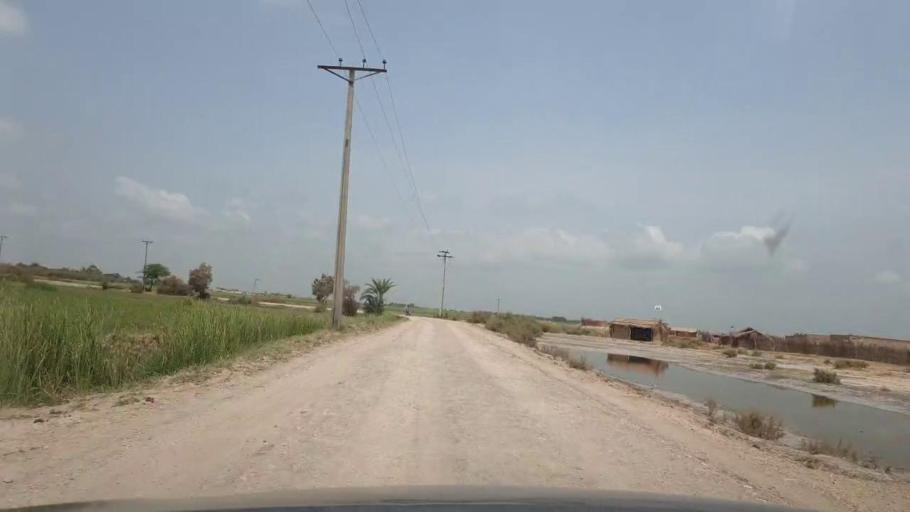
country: PK
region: Sindh
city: Ratodero
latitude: 27.9086
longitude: 68.3092
